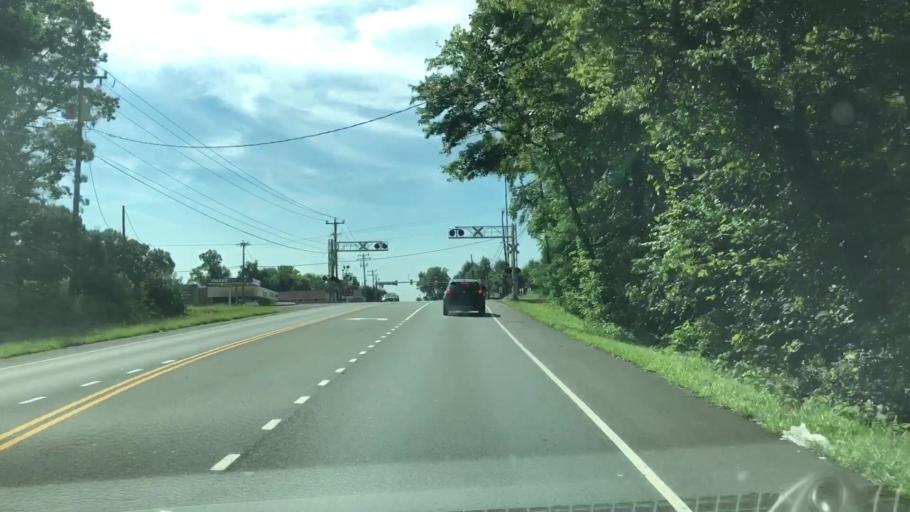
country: US
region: Virginia
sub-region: City of Fredericksburg
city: Fredericksburg
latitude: 38.2735
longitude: -77.4492
